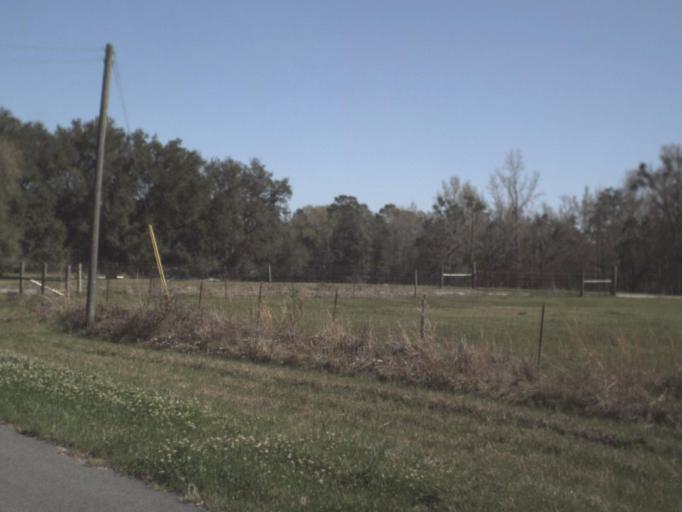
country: US
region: Florida
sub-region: Jefferson County
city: Monticello
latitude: 30.4681
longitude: -84.0197
